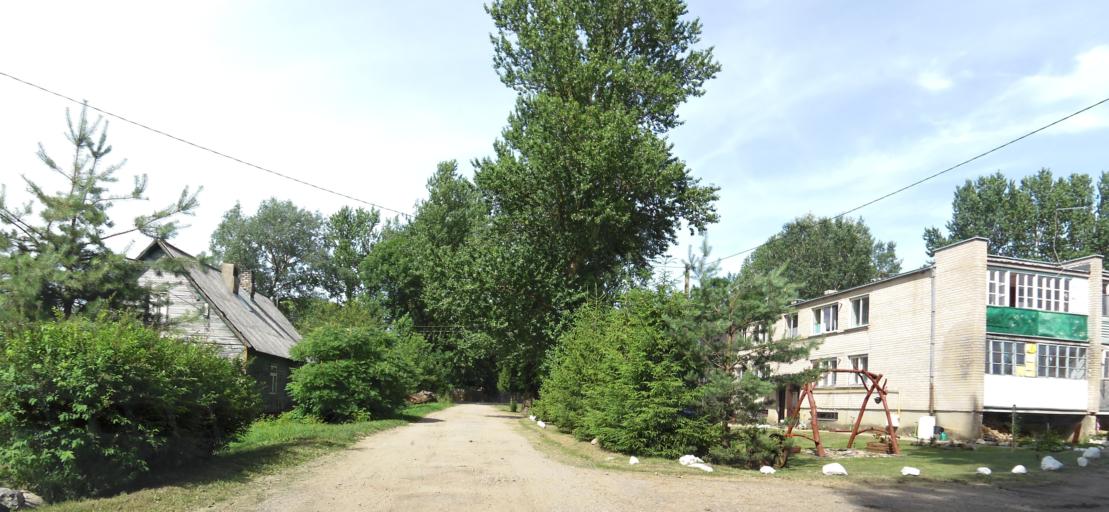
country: LT
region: Panevezys
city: Pasvalys
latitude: 55.9175
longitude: 24.2942
